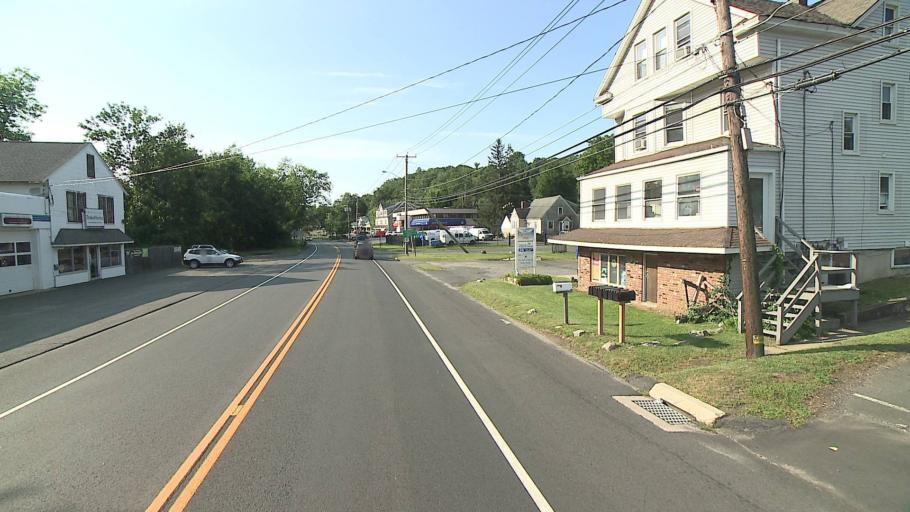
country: US
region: Connecticut
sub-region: Fairfield County
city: Georgetown
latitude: 41.2665
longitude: -73.4414
